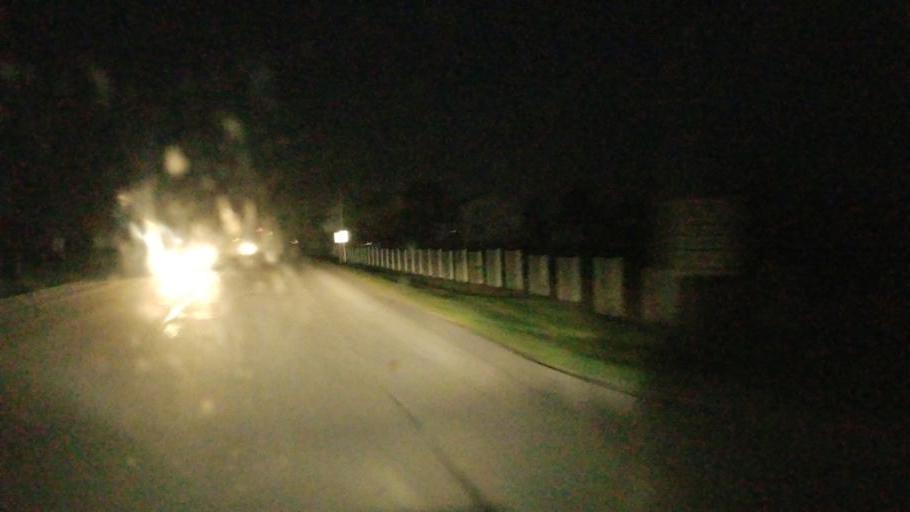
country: US
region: Indiana
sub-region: Elkhart County
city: Middlebury
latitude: 41.6758
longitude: -85.6486
